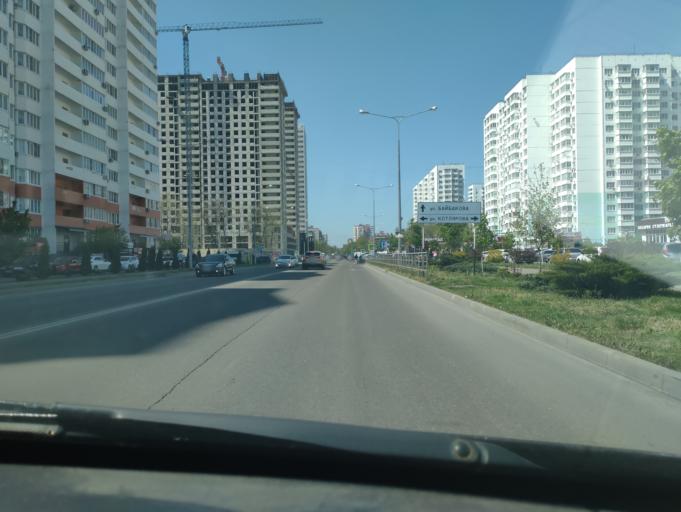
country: RU
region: Krasnodarskiy
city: Krasnodar
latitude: 45.0628
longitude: 39.0135
